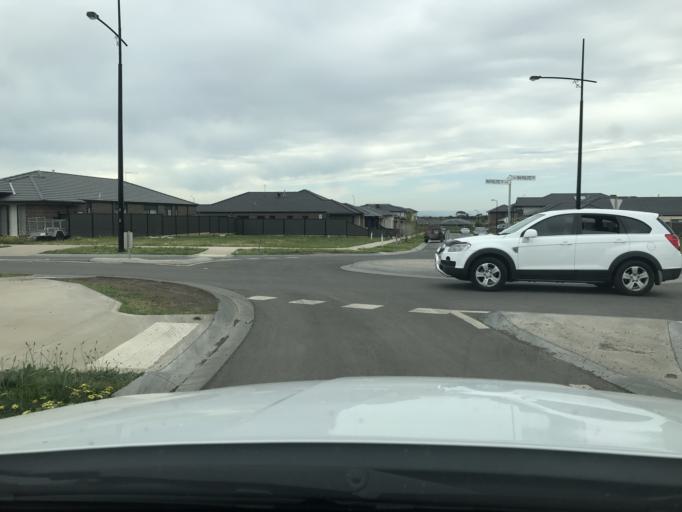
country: AU
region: Victoria
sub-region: Hume
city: Roxburgh Park
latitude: -37.6049
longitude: 144.9084
